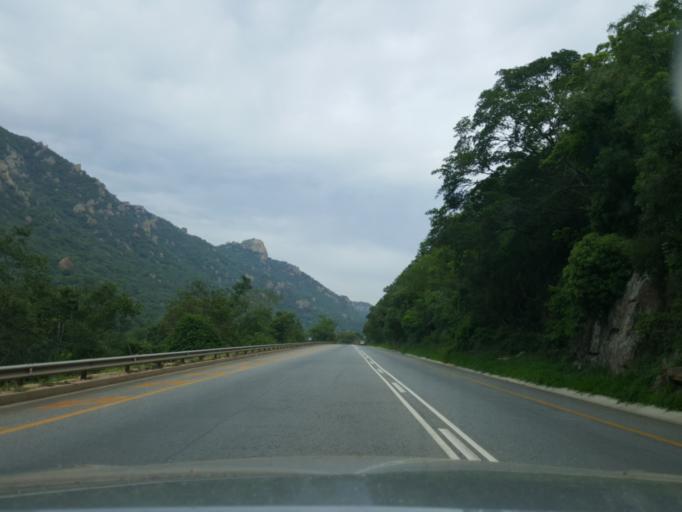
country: ZA
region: Mpumalanga
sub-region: Ehlanzeni District
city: Nelspruit
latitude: -25.5119
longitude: 31.2200
